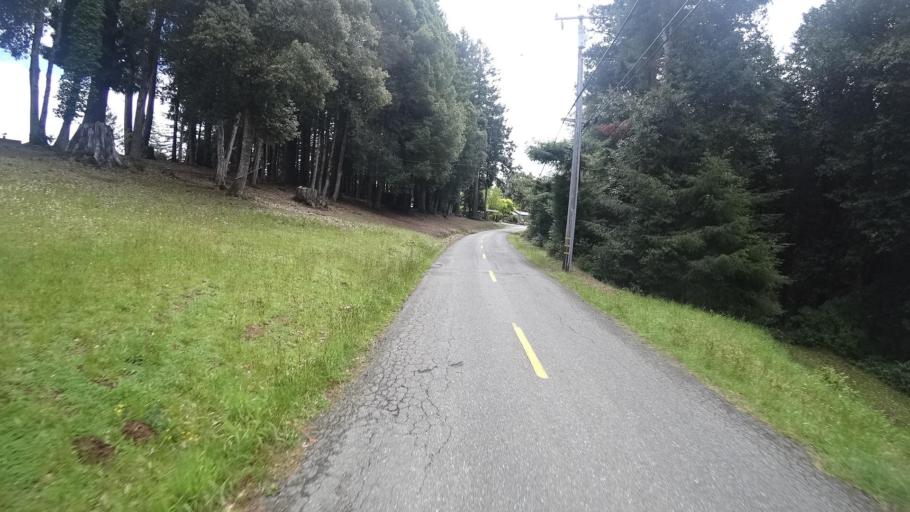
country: US
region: California
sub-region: Humboldt County
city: Bayside
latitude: 40.7705
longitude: -124.0002
